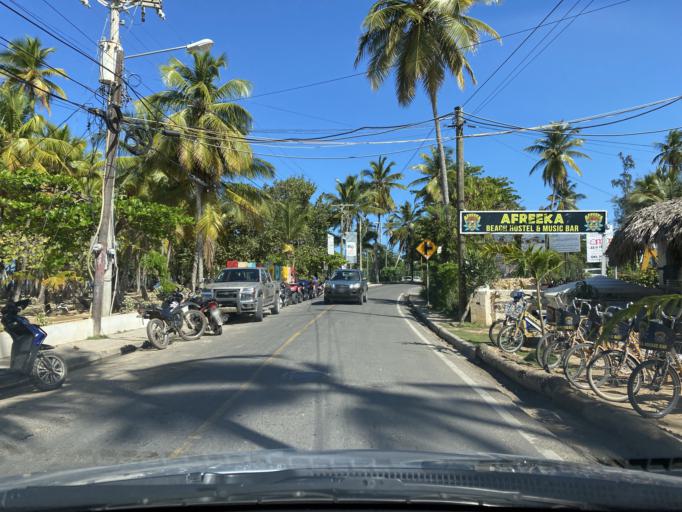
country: DO
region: Samana
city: Las Terrenas
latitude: 19.3249
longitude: -69.5299
